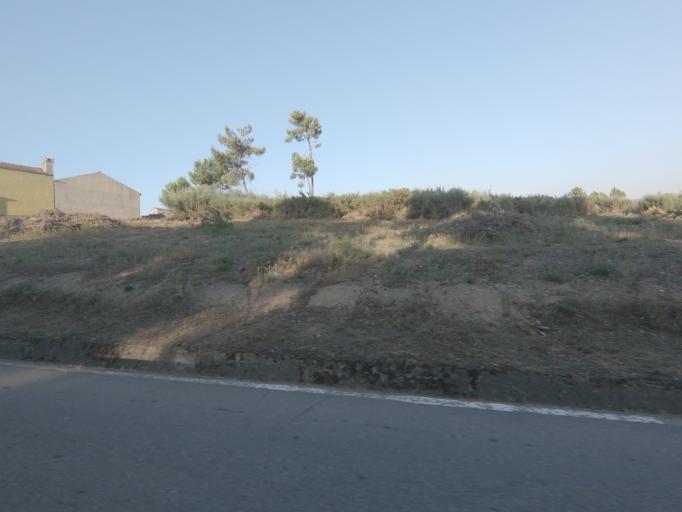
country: PT
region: Viseu
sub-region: Armamar
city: Armamar
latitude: 41.1975
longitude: -7.6918
